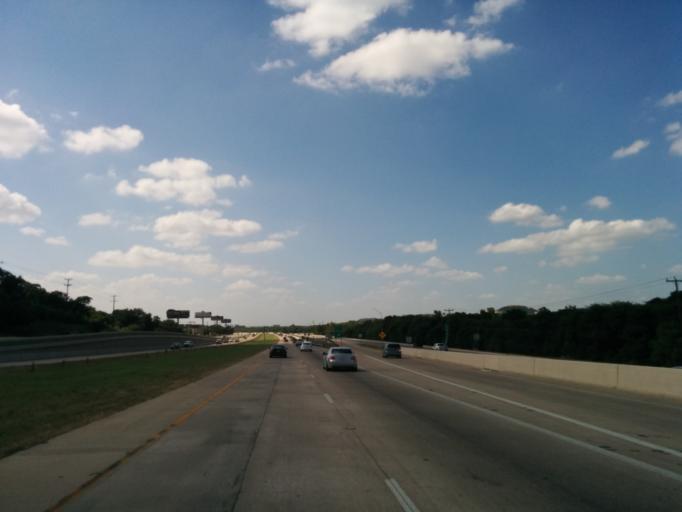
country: US
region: Texas
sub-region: Bexar County
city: Cross Mountain
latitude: 29.6276
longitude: -98.6107
